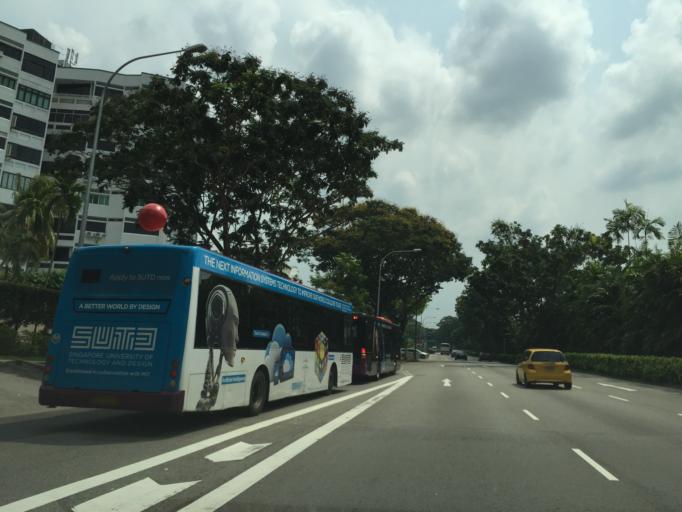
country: SG
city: Singapore
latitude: 1.3214
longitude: 103.8229
